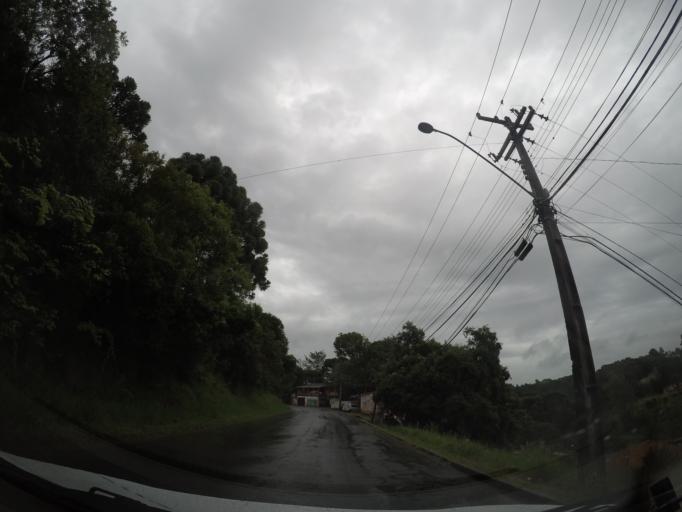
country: BR
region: Parana
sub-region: Curitiba
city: Curitiba
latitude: -25.4608
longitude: -49.3914
